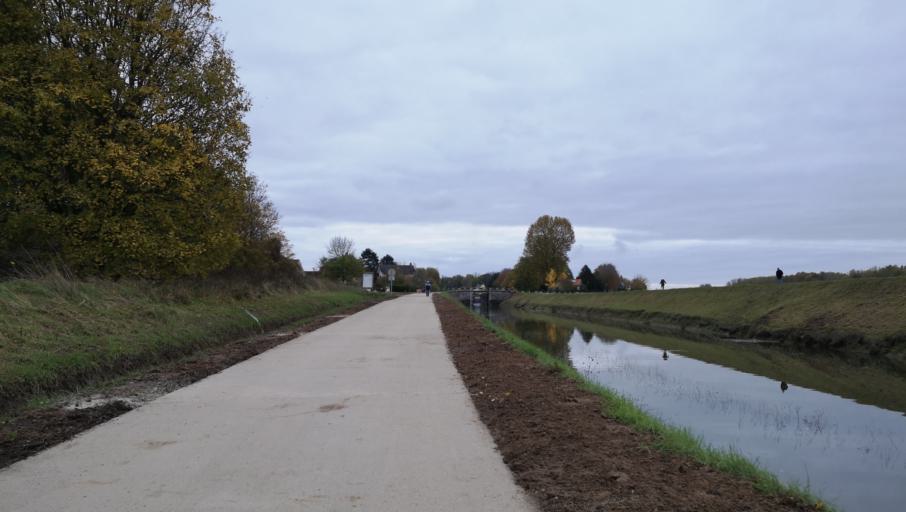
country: FR
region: Centre
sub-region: Departement du Loiret
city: Saint-Jean-de-Braye
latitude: 47.9018
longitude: 1.9813
